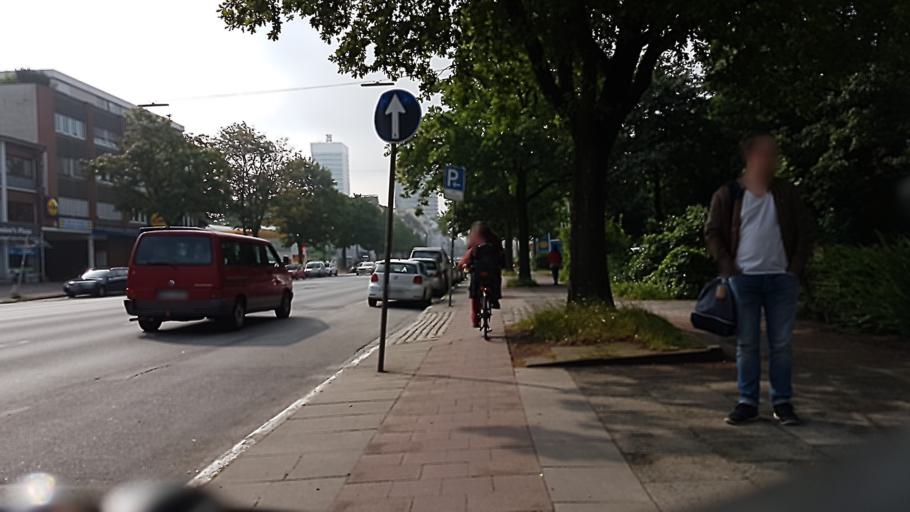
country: DE
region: Hamburg
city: Hamburg
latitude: 53.5746
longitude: 10.0218
